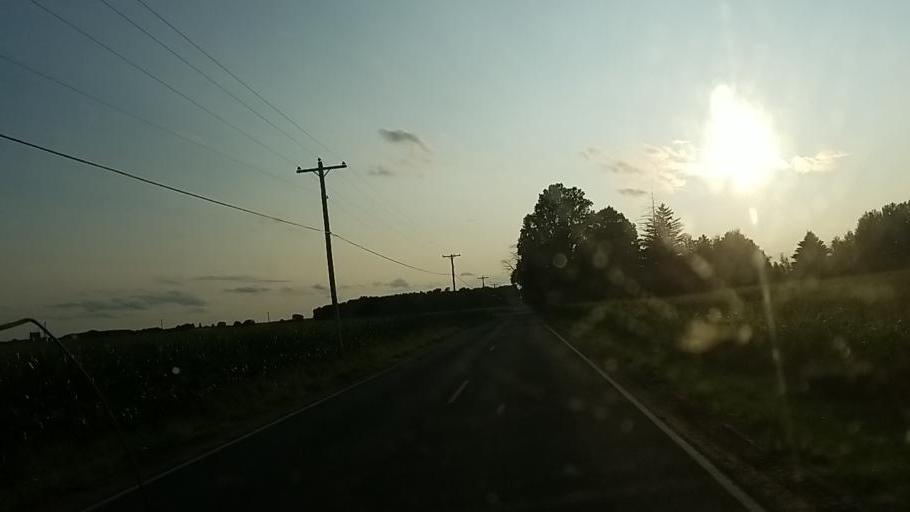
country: US
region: Michigan
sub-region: Montcalm County
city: Howard City
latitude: 43.3666
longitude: -85.4181
